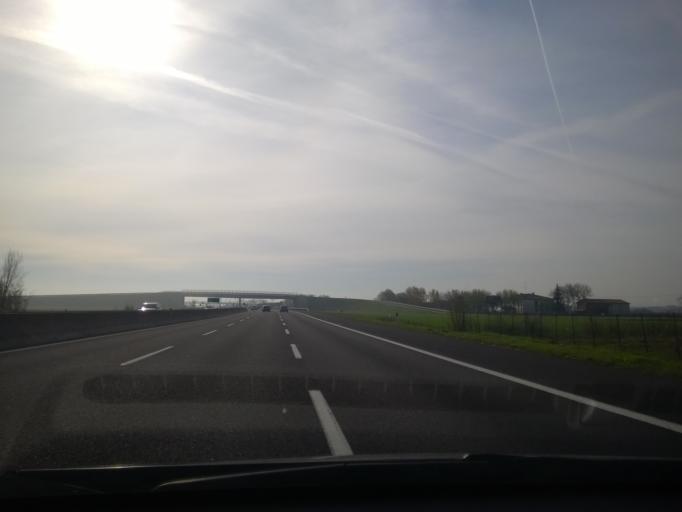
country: IT
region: Emilia-Romagna
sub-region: Provincia di Bologna
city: Imola
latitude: 44.3931
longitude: 11.7079
